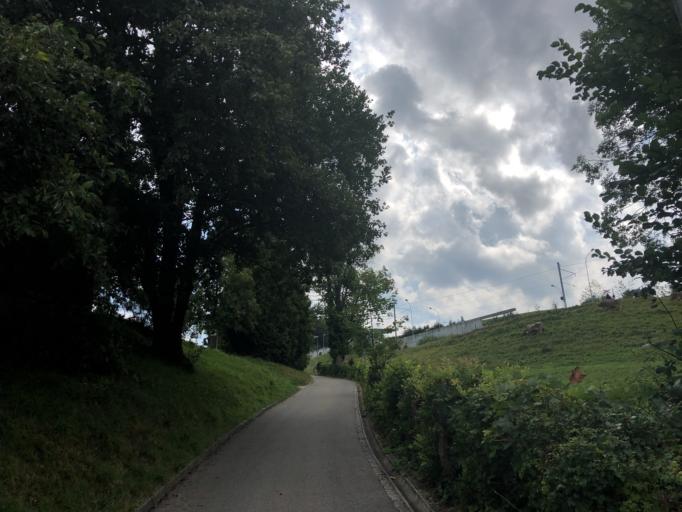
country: CH
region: Saint Gallen
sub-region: Wahlkreis St. Gallen
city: Sankt Gallen
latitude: 47.4262
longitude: 9.3915
